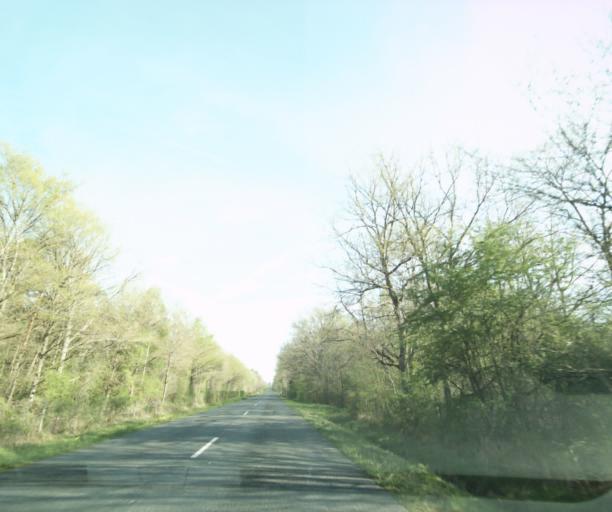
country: FR
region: Ile-de-France
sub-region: Departement de Seine-et-Marne
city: Vernou-la-Celle-sur-Seine
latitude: 48.4225
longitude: 2.8488
